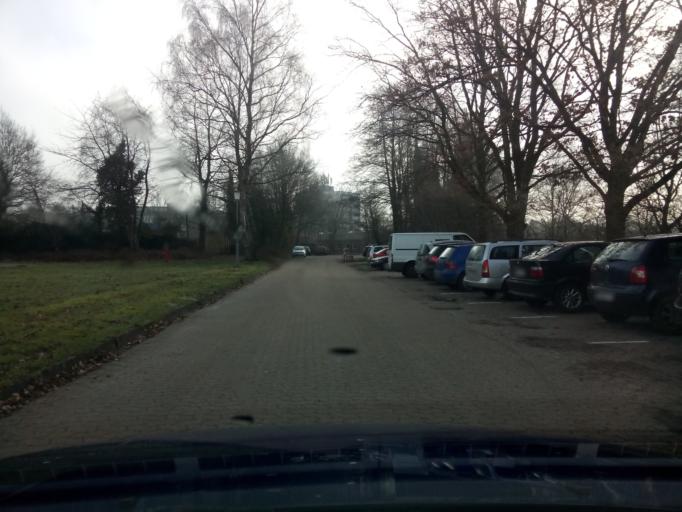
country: DE
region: Lower Saxony
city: Lilienthal
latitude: 53.1471
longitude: 8.9050
